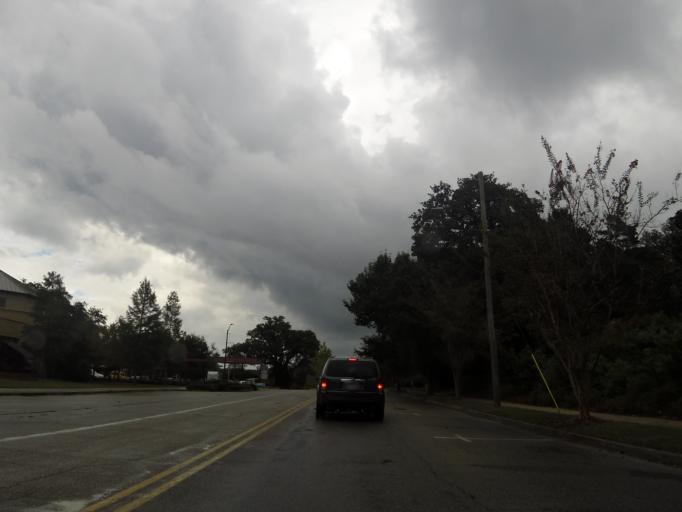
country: US
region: Alabama
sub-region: Baldwin County
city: Fairhope
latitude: 30.5230
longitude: -87.9017
